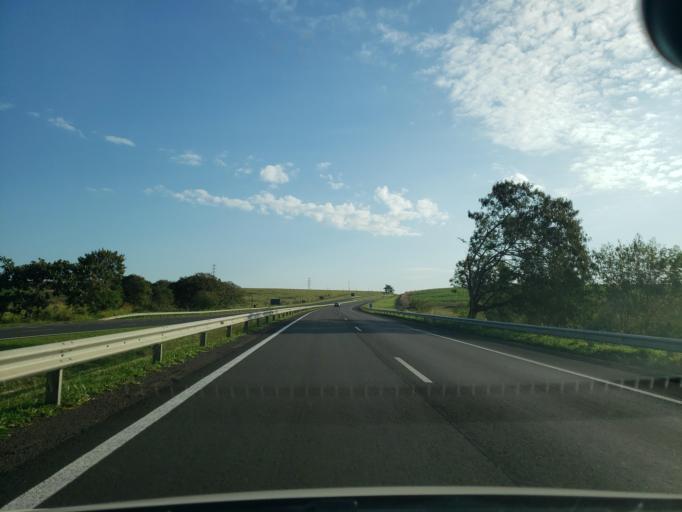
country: BR
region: Sao Paulo
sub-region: Valparaiso
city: Valparaiso
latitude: -21.2159
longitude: -50.8415
